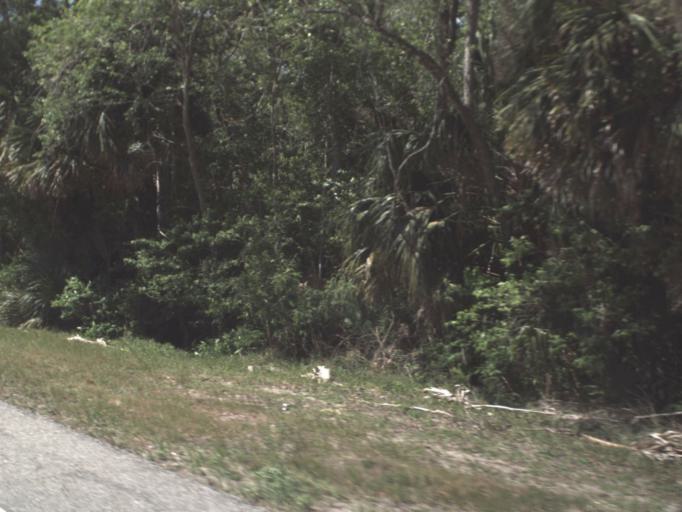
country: US
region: Florida
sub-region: Flagler County
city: Palm Coast
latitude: 29.6496
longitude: -81.2868
